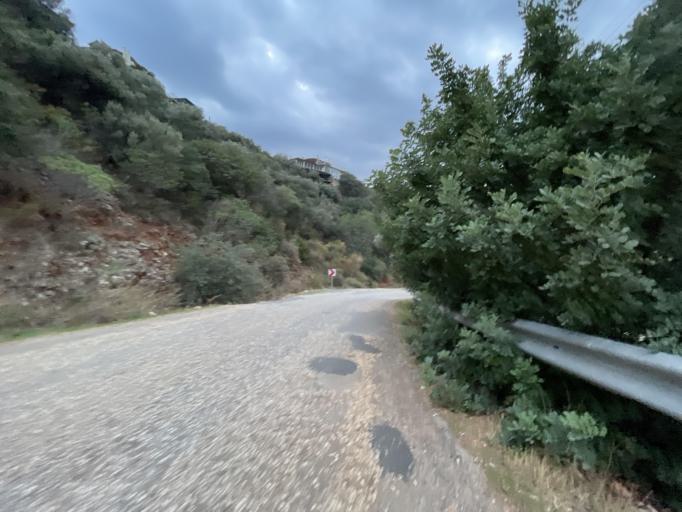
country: TR
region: Antalya
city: Kas
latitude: 36.1906
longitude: 29.6541
